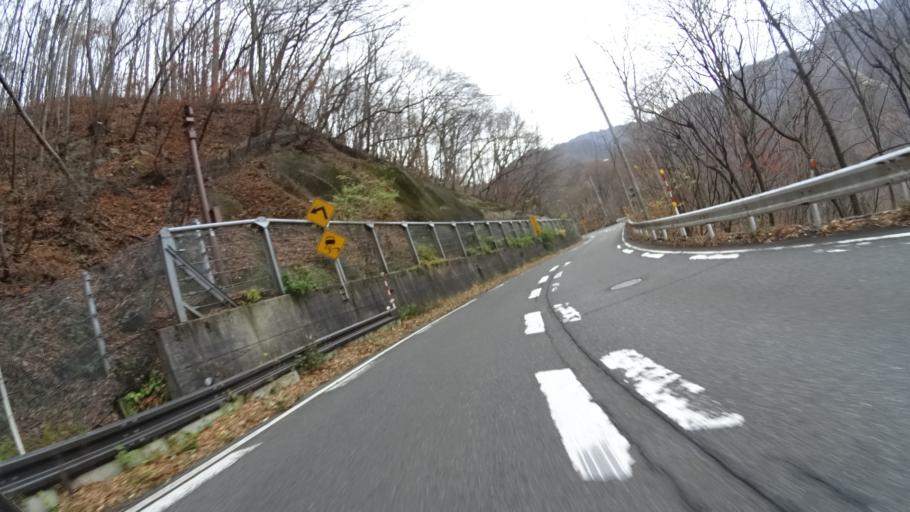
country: JP
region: Gunma
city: Nakanojomachi
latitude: 36.7316
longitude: 138.8397
